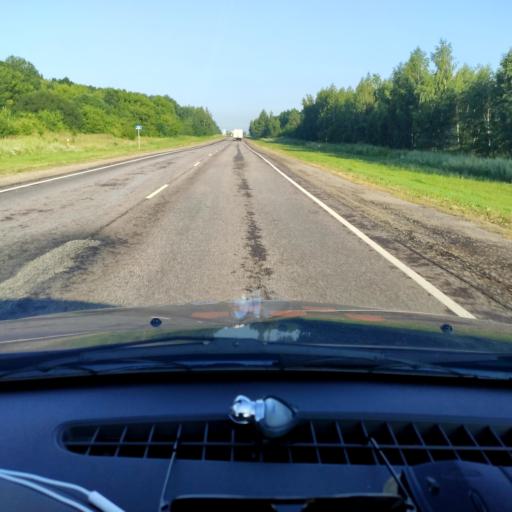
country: RU
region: Lipetsk
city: Izmalkovo
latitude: 52.4370
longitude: 37.9006
